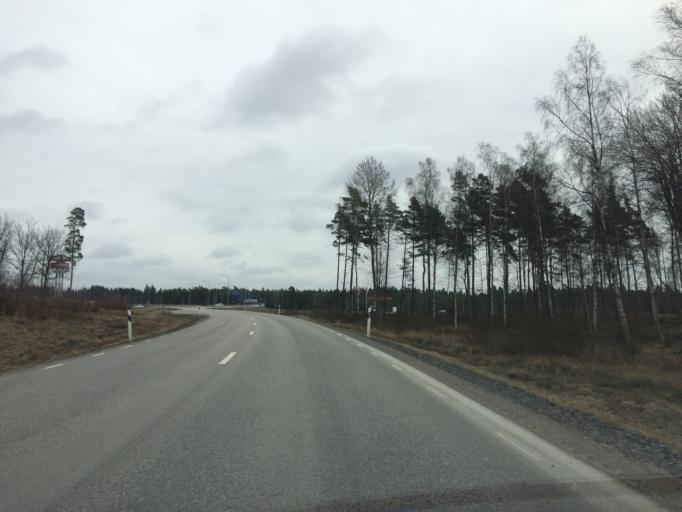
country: SE
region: Kronoberg
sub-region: Almhults Kommun
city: AElmhult
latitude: 56.5484
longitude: 14.1529
